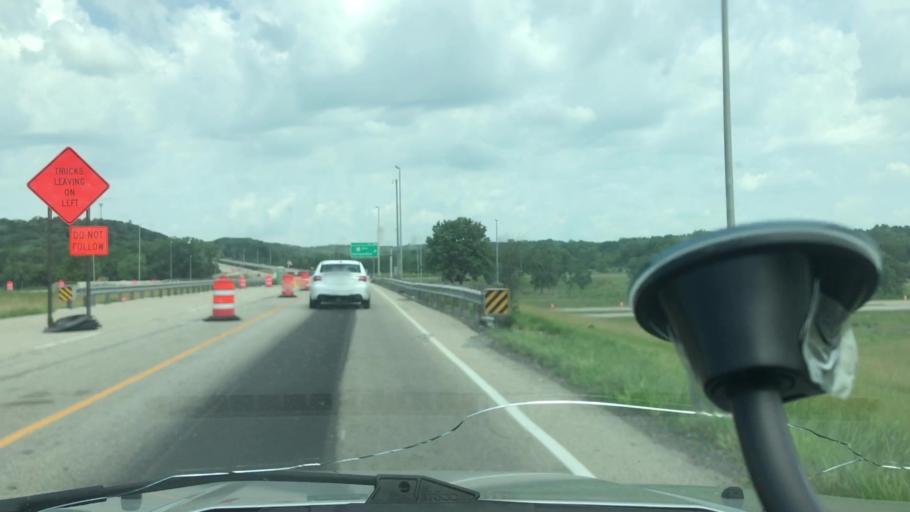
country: US
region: Illinois
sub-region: Peoria County
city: Bartonville
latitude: 40.6557
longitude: -89.6423
